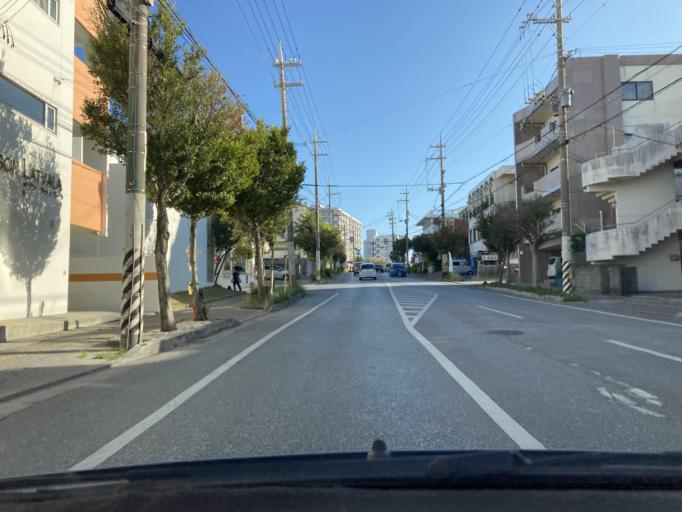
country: JP
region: Okinawa
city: Ginowan
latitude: 26.2555
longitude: 127.7136
